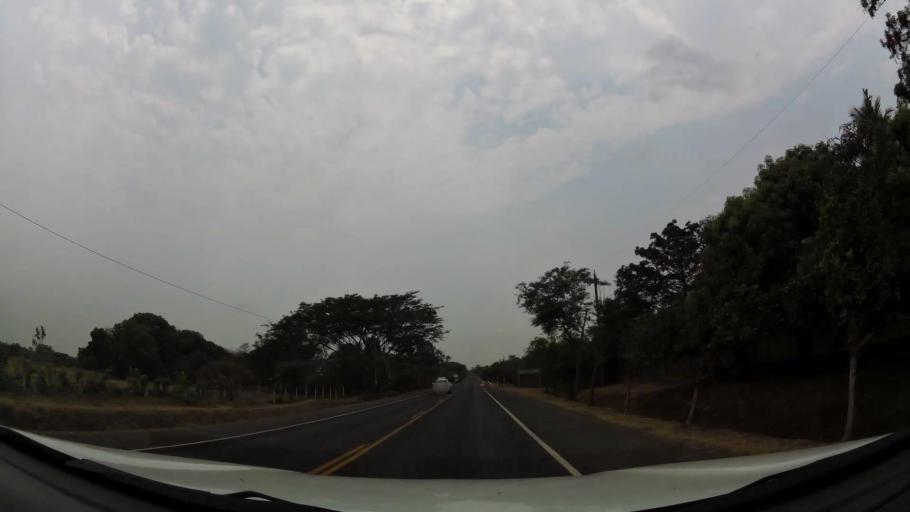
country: NI
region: Chinandega
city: Chichigalpa
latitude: 12.6004
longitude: -87.0430
